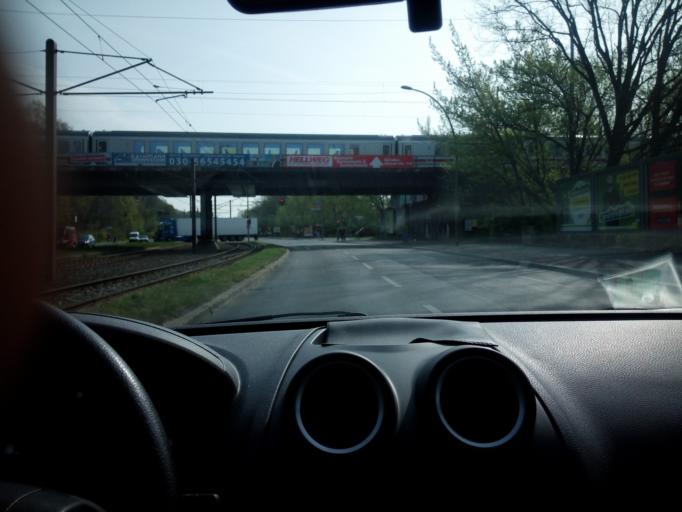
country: DE
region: Berlin
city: Adlershof
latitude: 52.4578
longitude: 13.5545
